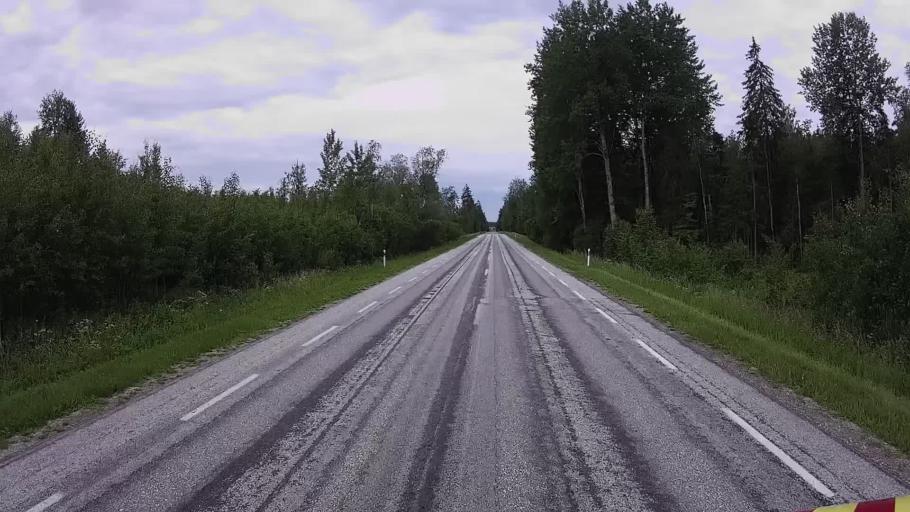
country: EE
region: Viljandimaa
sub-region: Karksi vald
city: Karksi-Nuia
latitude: 58.1923
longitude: 25.6079
